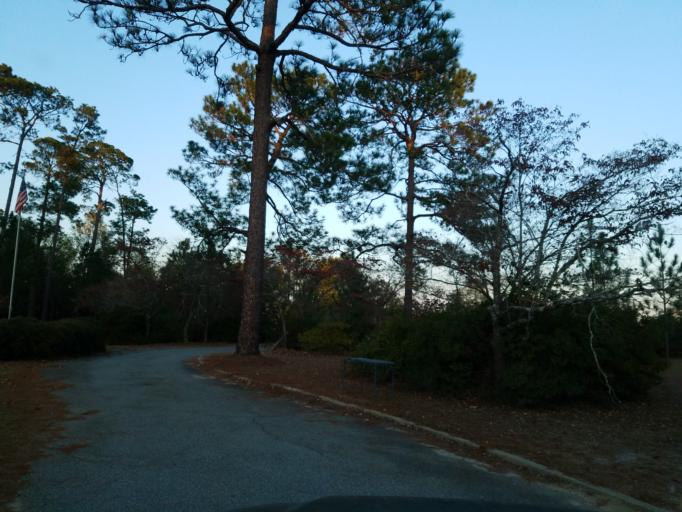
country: US
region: Georgia
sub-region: Ben Hill County
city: Fitzgerald
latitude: 31.6637
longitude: -83.3869
